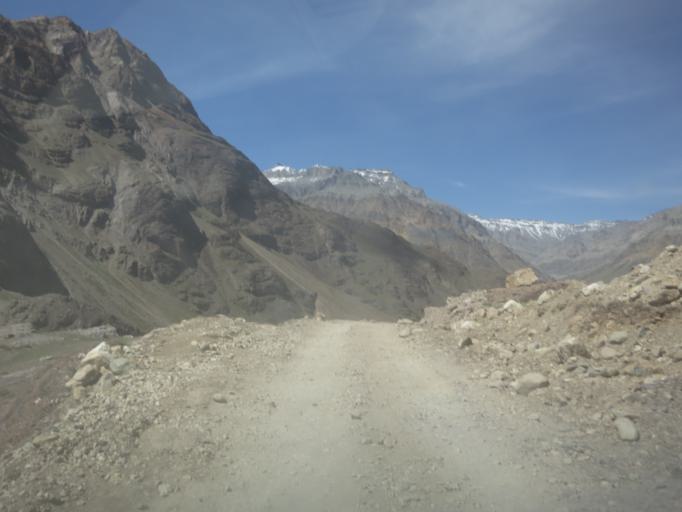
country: IN
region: Himachal Pradesh
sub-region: Kulu
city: Manali
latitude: 32.4331
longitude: 77.6755
